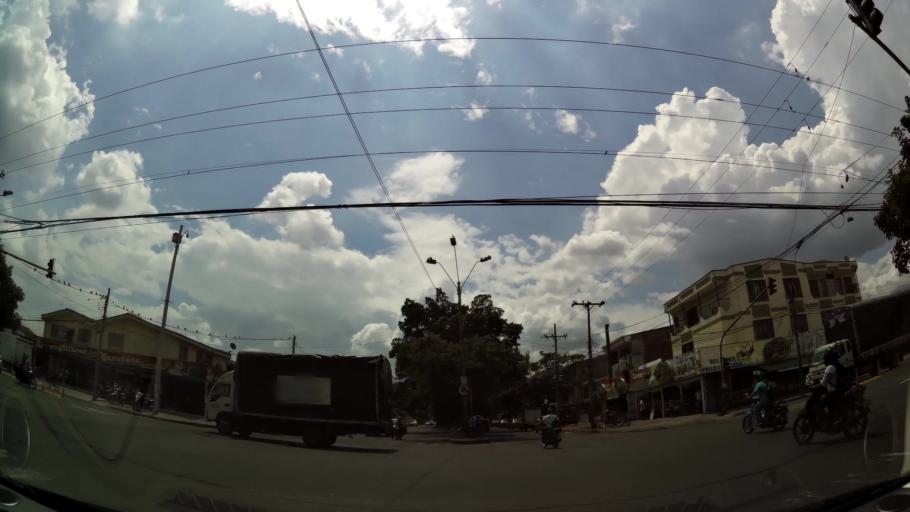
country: CO
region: Valle del Cauca
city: Cali
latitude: 3.4675
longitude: -76.5039
